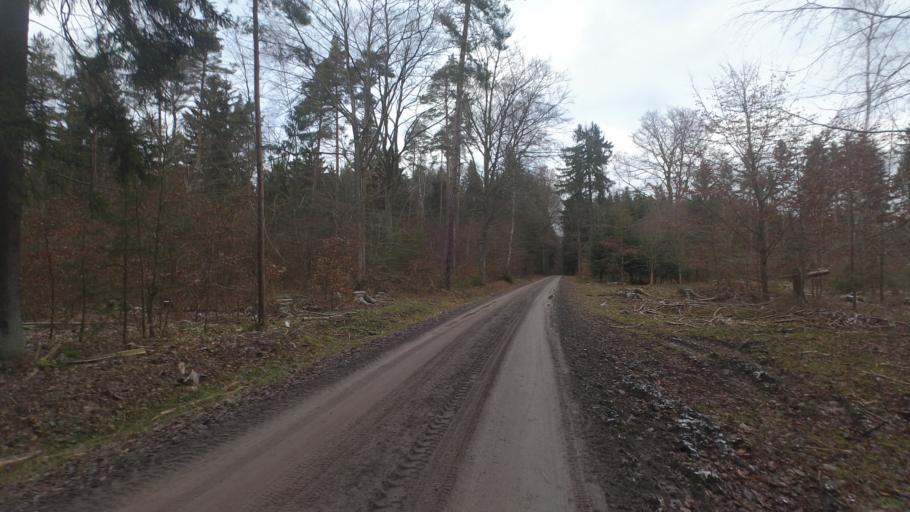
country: DE
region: Thuringia
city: Konitz
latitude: 50.6901
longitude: 11.4617
